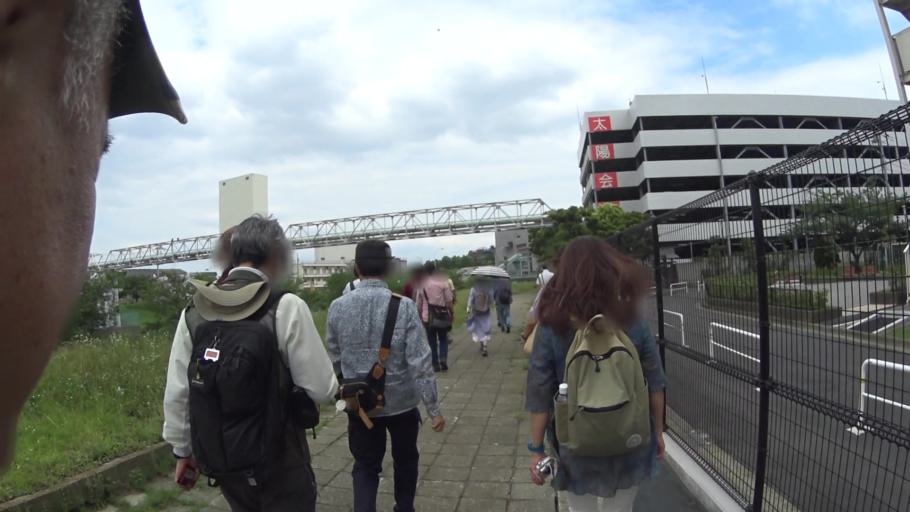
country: JP
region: Tokyo
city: Urayasu
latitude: 35.7176
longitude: 139.8370
